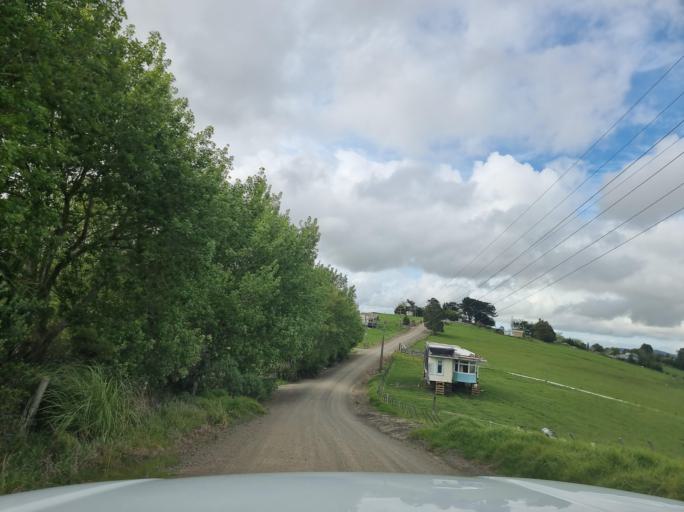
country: NZ
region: Northland
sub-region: Whangarei
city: Ruakaka
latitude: -36.1283
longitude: 174.2082
